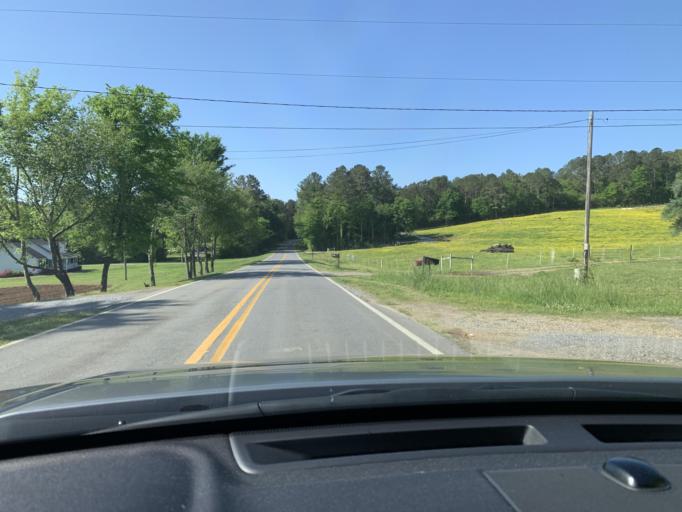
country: US
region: Georgia
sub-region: Polk County
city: Cedartown
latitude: 34.0271
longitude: -85.3007
